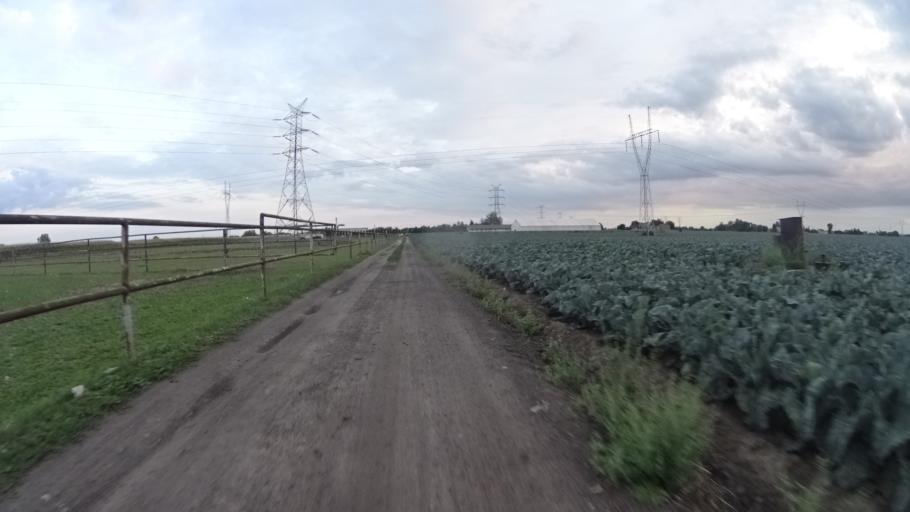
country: PL
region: Masovian Voivodeship
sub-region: Powiat warszawski zachodni
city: Ozarow Mazowiecki
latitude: 52.2390
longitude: 20.7660
